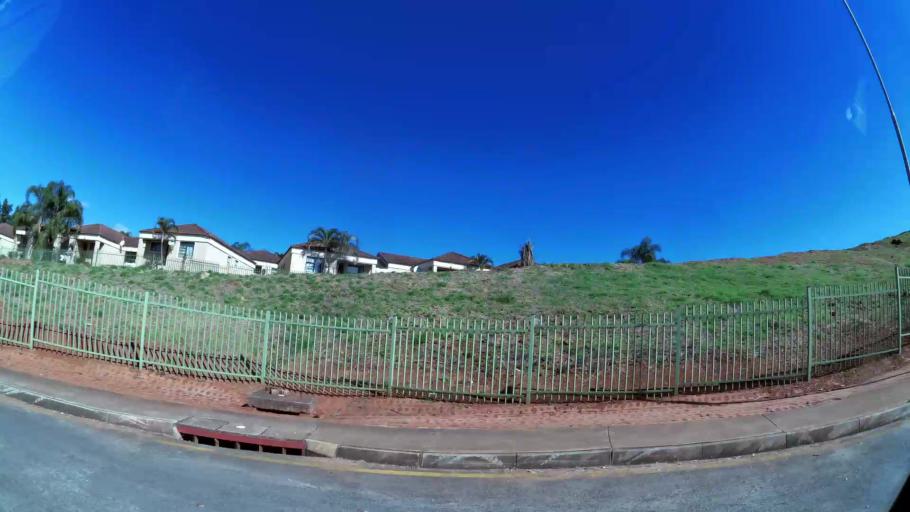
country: ZA
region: Limpopo
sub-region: Mopani District Municipality
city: Tzaneen
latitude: -23.8241
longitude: 30.1541
